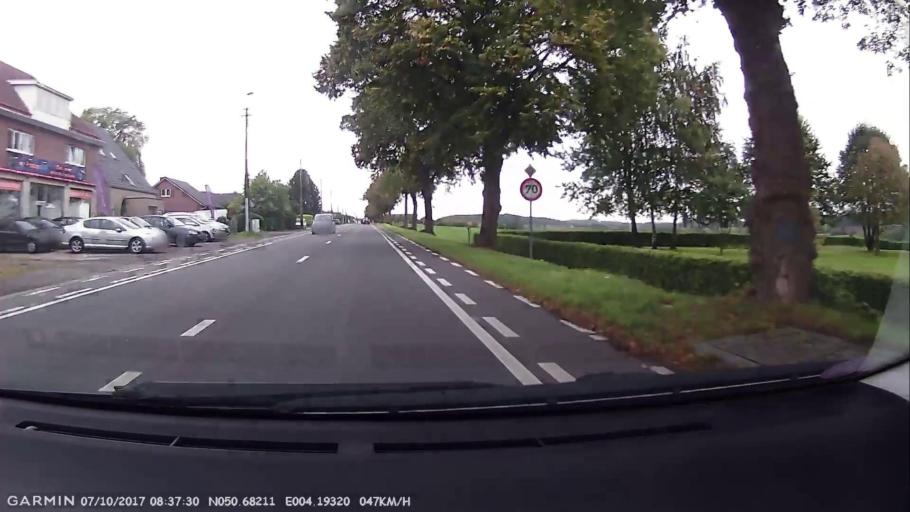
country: BE
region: Wallonia
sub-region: Province du Brabant Wallon
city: Tubize
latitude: 50.6819
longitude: 4.1931
